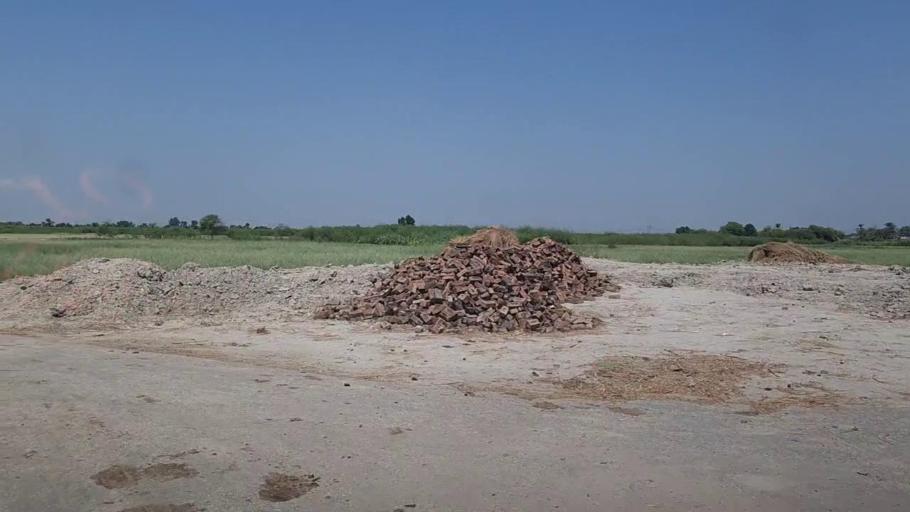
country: PK
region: Sindh
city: Ubauro
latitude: 28.2034
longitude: 69.8035
